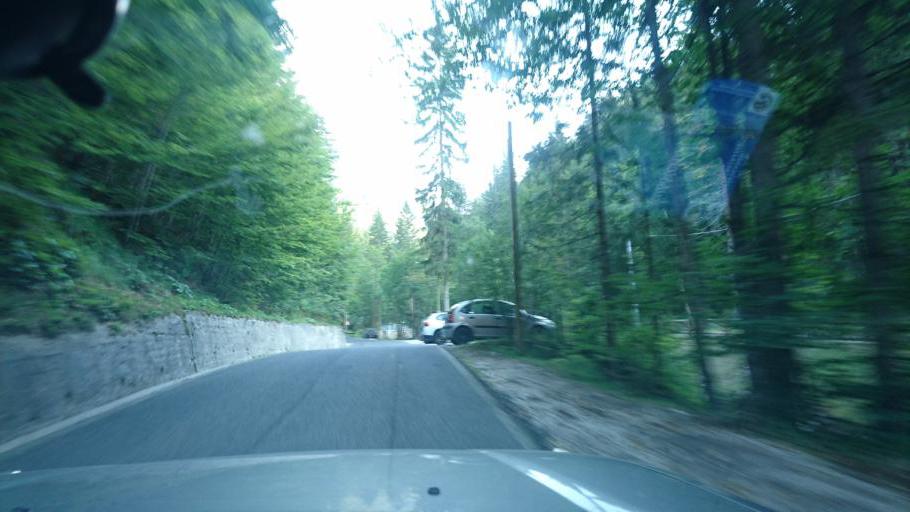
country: AT
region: Carinthia
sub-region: Politischer Bezirk Villach Land
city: Arnoldstein
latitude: 46.4877
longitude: 13.6728
